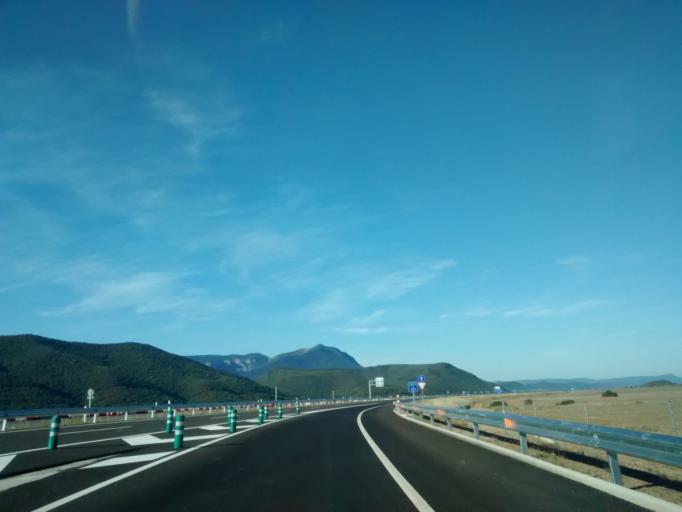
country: ES
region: Aragon
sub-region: Provincia de Huesca
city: Jaca
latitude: 42.5642
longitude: -0.6033
